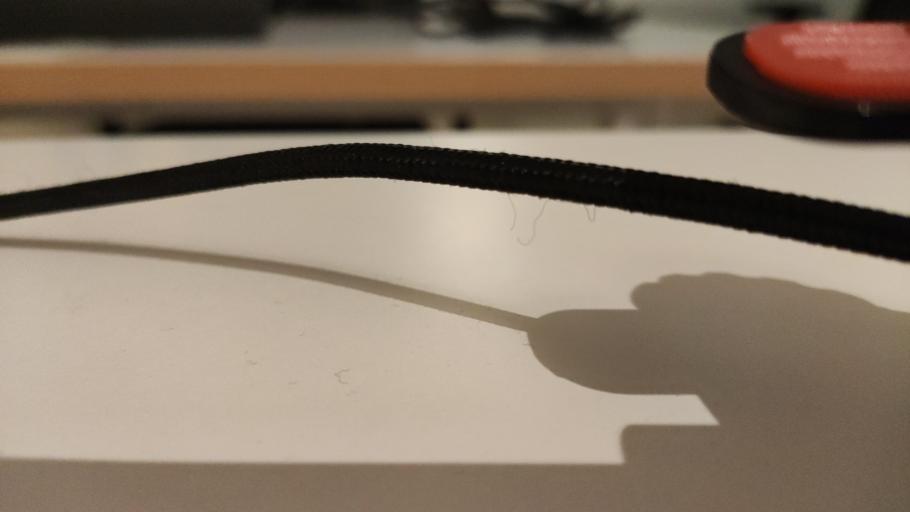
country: RU
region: Moskovskaya
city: Kurovskoye
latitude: 55.5393
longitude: 38.8729
